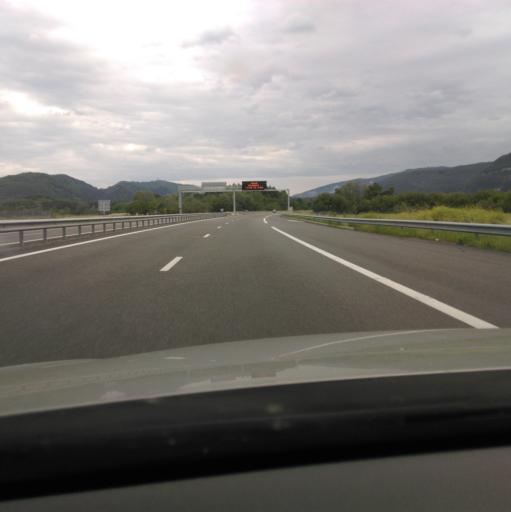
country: FR
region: Rhone-Alpes
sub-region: Departement de l'Ain
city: Saint-Martin-du-Frene
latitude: 46.1583
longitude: 5.5497
